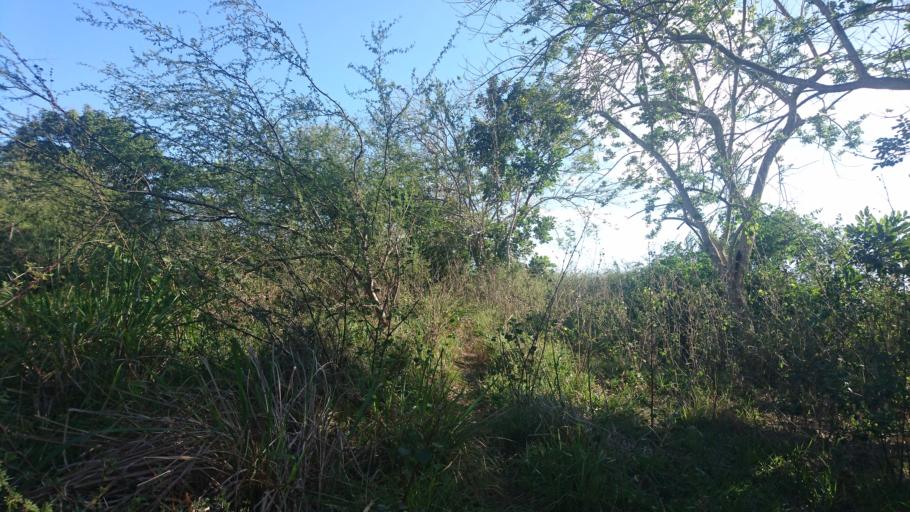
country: CU
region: Artemisa
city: Soroa
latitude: 22.8272
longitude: -82.9216
